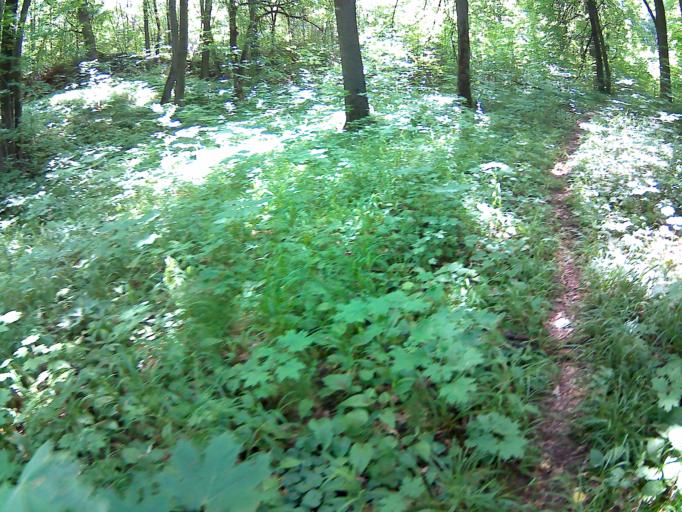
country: RU
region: Nizjnij Novgorod
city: Nizhniy Novgorod
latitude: 56.2292
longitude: 43.9245
